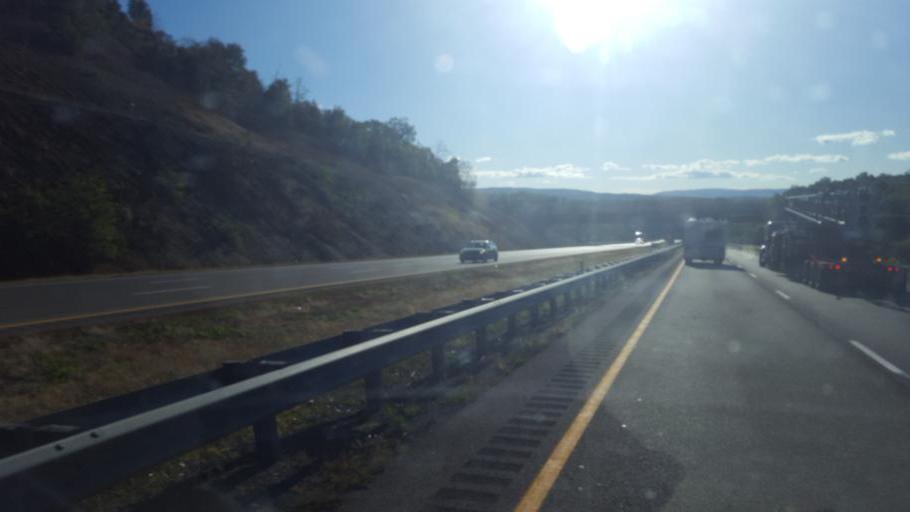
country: US
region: Maryland
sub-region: Allegany County
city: Cumberland
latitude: 39.6953
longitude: -78.5118
